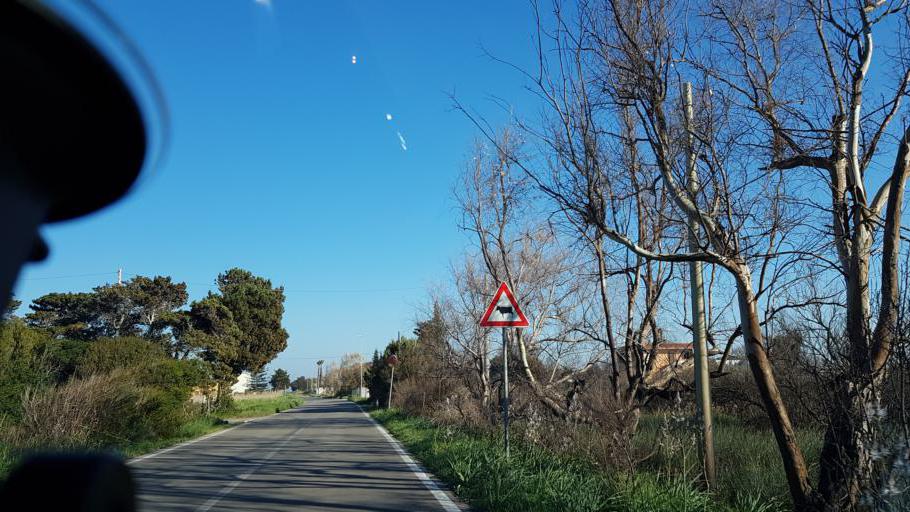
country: IT
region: Apulia
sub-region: Provincia di Lecce
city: Giorgilorio
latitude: 40.4510
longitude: 18.2217
